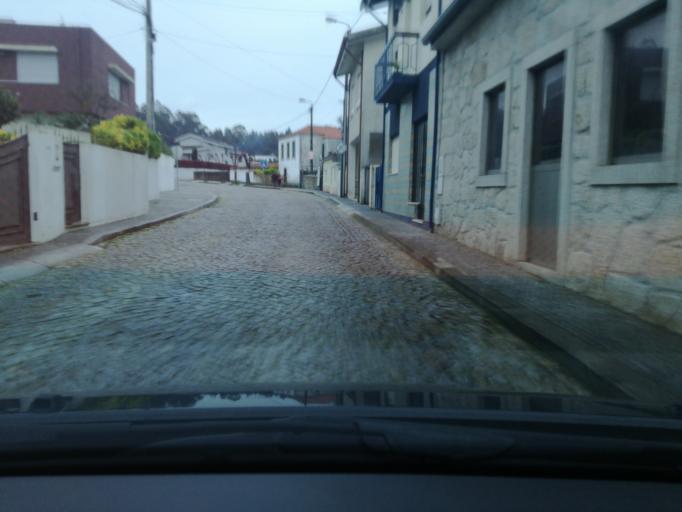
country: PT
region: Porto
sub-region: Maia
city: Gemunde
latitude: 41.2663
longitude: -8.6424
